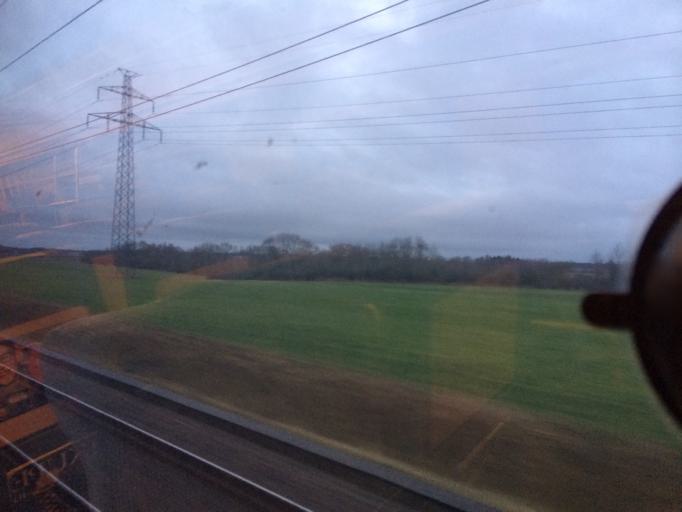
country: SE
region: Skane
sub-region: Kavlinge Kommun
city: Hofterup
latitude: 55.8366
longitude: 12.9809
